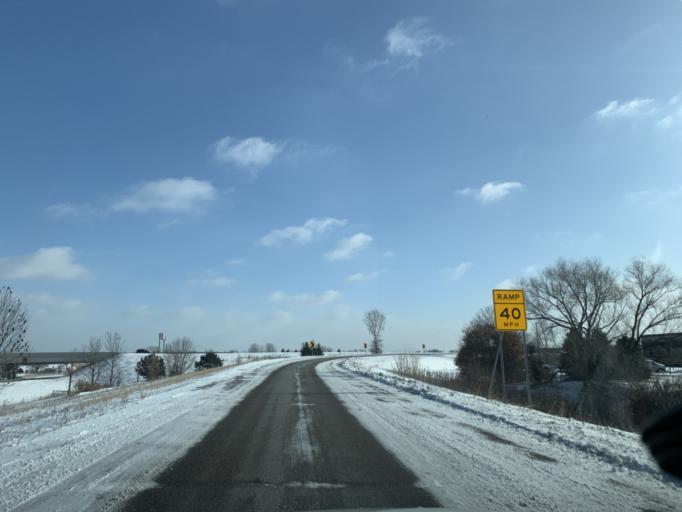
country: US
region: Minnesota
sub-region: Scott County
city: Prior Lake
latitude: 44.7830
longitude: -93.4157
